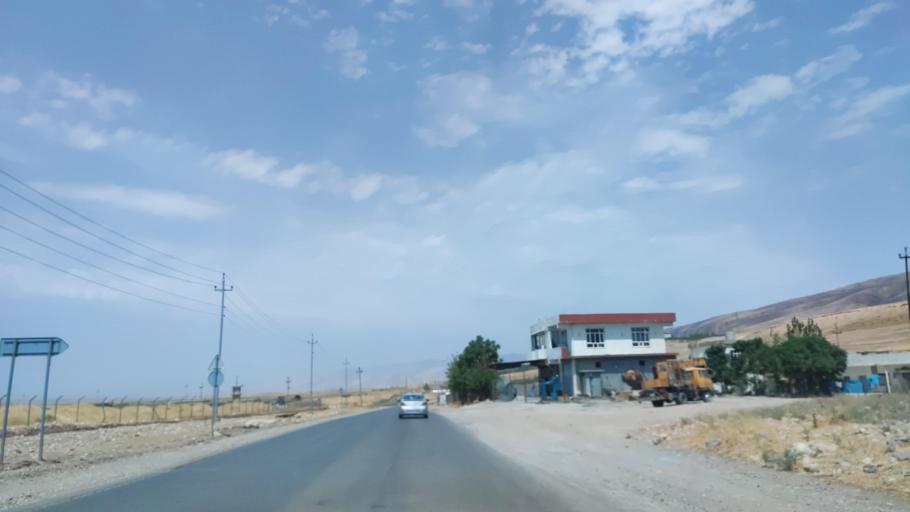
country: IQ
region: Arbil
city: Shaqlawah
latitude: 36.5299
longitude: 44.3586
